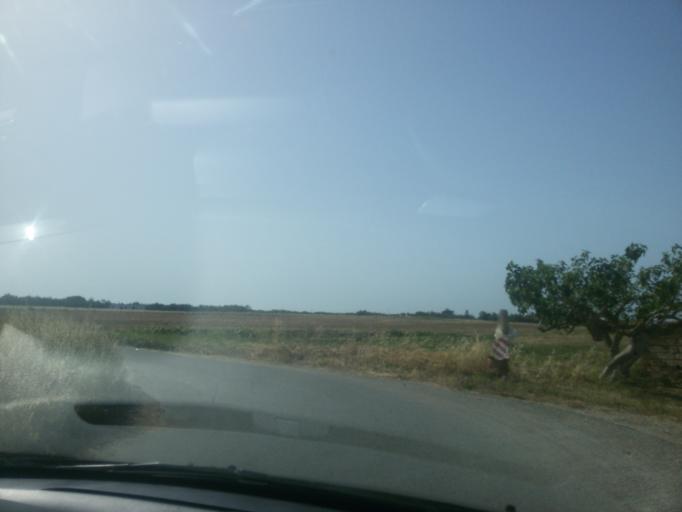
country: IT
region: Apulia
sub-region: Provincia di Brindisi
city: Brindisi
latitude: 40.6802
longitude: 17.8864
